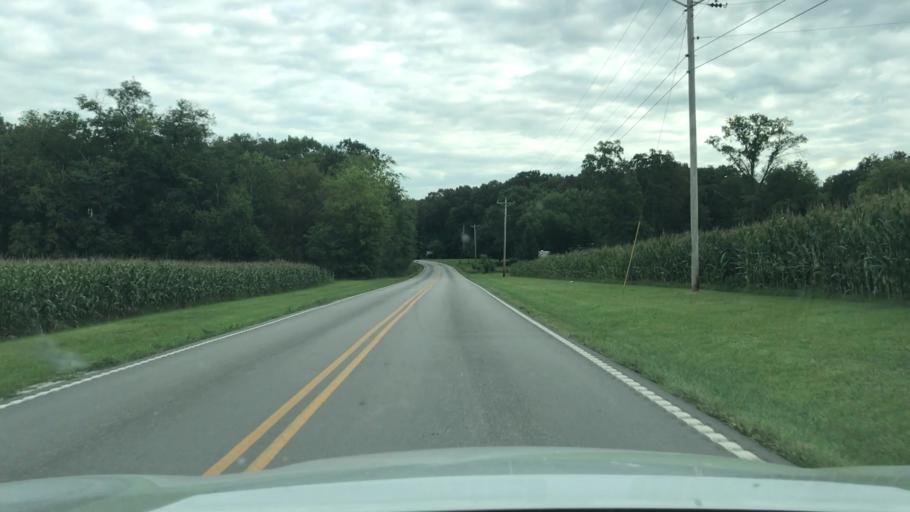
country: US
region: Kentucky
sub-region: Todd County
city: Guthrie
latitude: 36.7228
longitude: -87.1900
